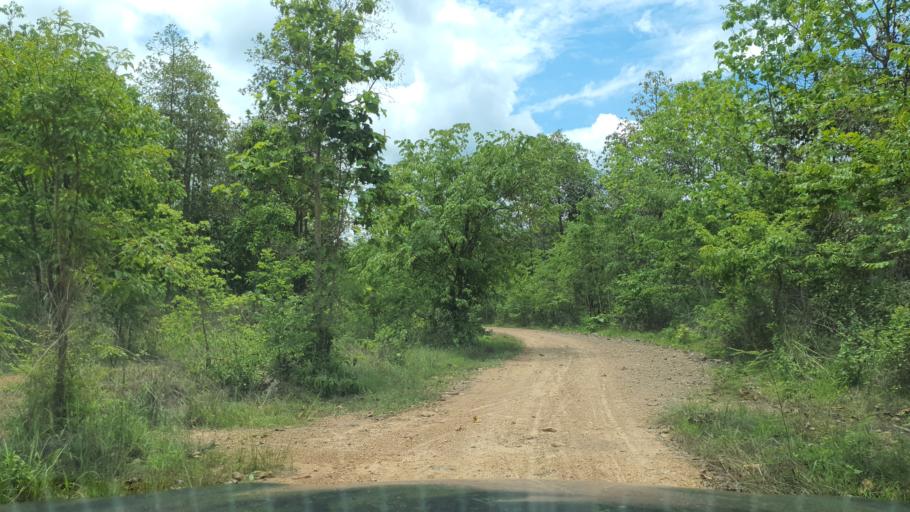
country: TH
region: Chiang Mai
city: San Sai
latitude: 18.9271
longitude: 99.0629
